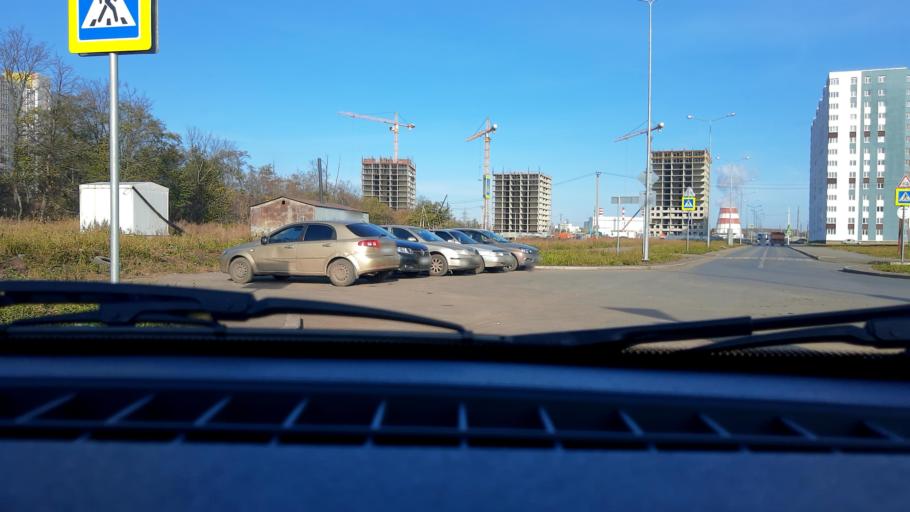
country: RU
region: Bashkortostan
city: Mikhaylovka
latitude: 54.7905
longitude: 55.8490
